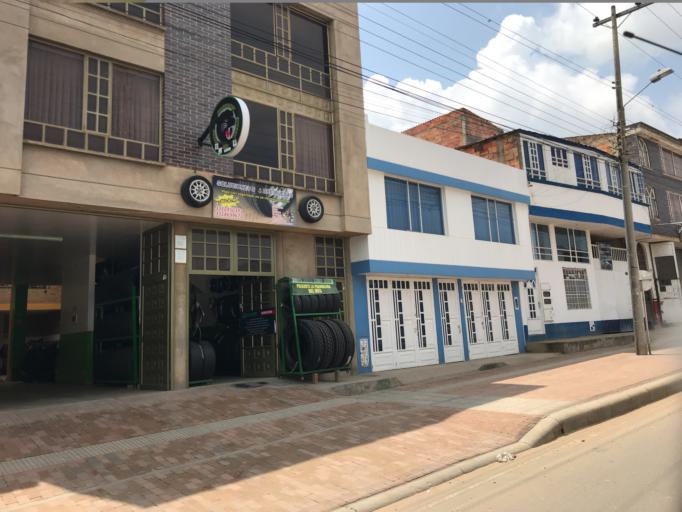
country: CO
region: Boyaca
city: Tunja
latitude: 5.5420
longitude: -73.3681
